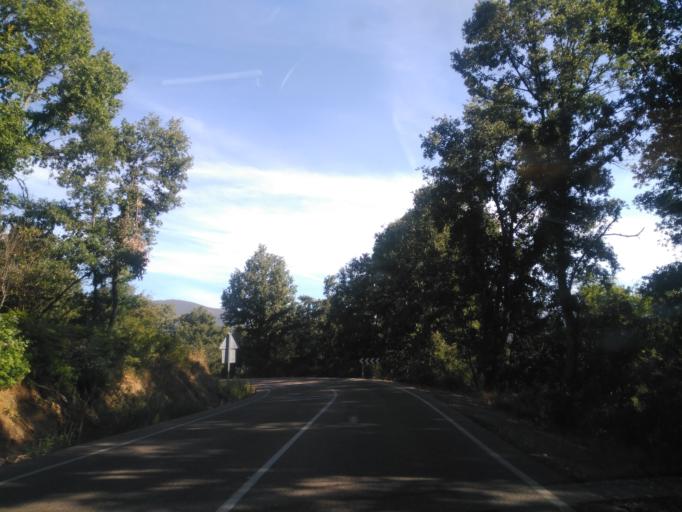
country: ES
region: Castille and Leon
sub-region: Provincia de Zamora
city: Galende
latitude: 42.1001
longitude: -6.6521
